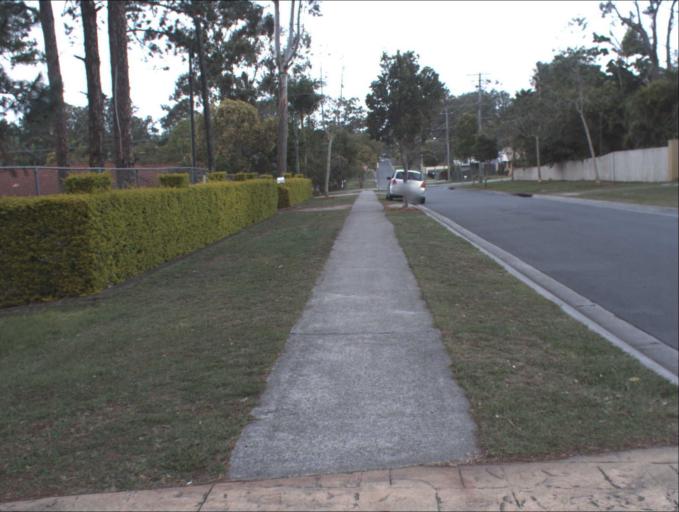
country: AU
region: Queensland
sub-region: Logan
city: Waterford West
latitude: -27.6820
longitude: 153.1243
